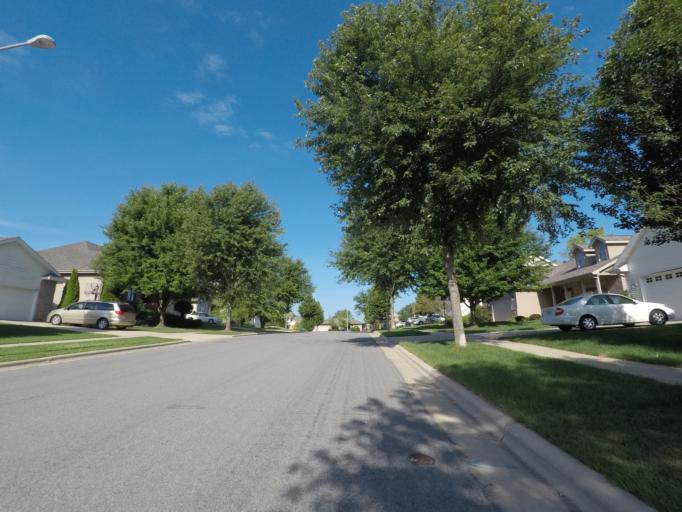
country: US
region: Wisconsin
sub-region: Dane County
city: Middleton
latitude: 43.0692
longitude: -89.5495
